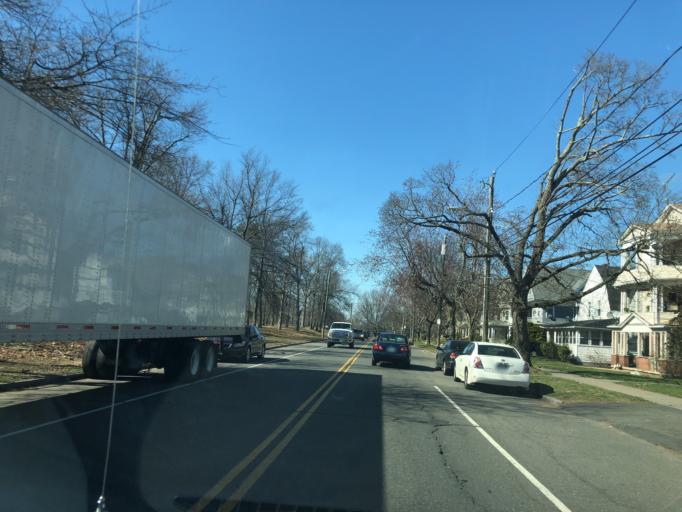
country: US
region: Connecticut
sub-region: Hartford County
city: Hartford
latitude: 41.7390
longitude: -72.6929
